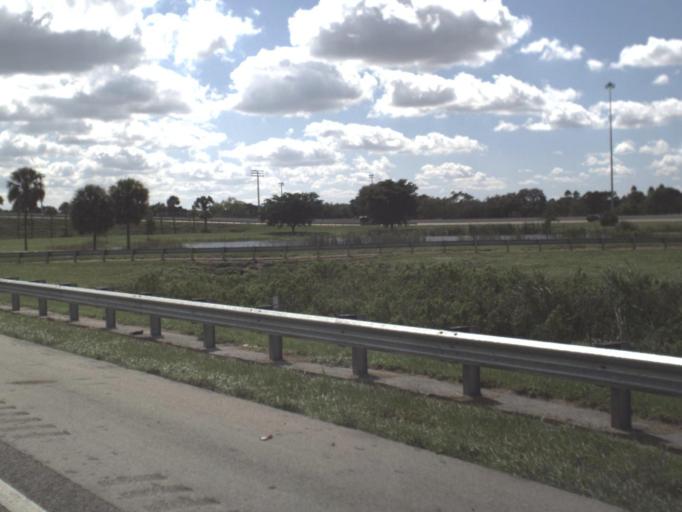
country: US
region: Florida
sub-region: Broward County
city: Coconut Creek
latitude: 26.2729
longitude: -80.1690
